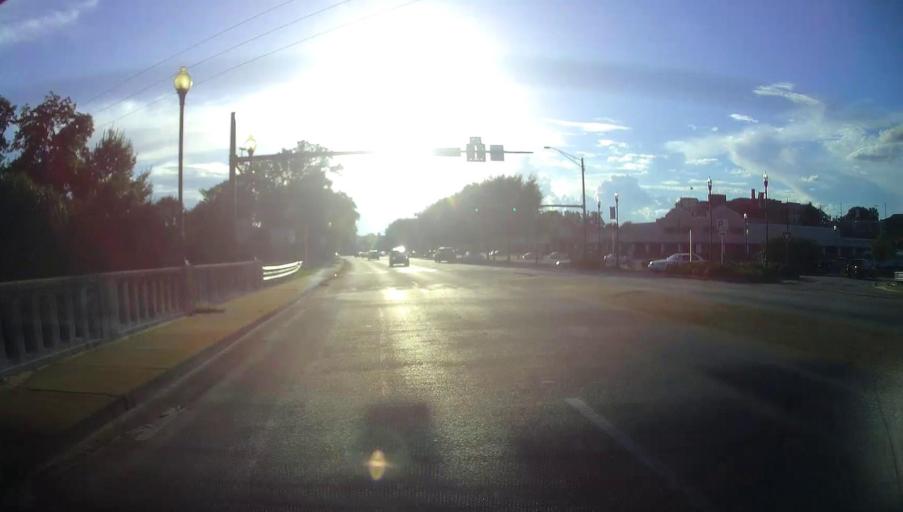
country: US
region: Alabama
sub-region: Russell County
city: Phenix City
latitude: 32.4713
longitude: -84.9975
